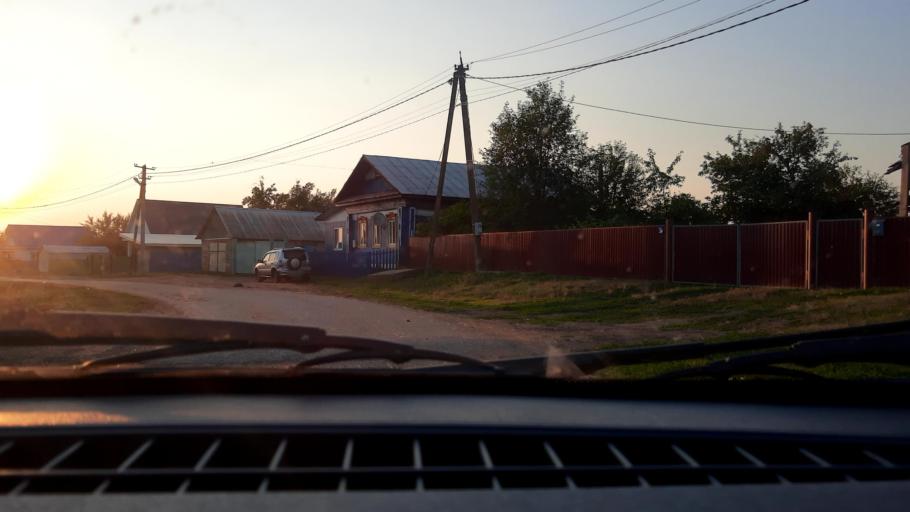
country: RU
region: Bashkortostan
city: Blagoveshchensk
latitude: 54.9428
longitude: 55.8803
